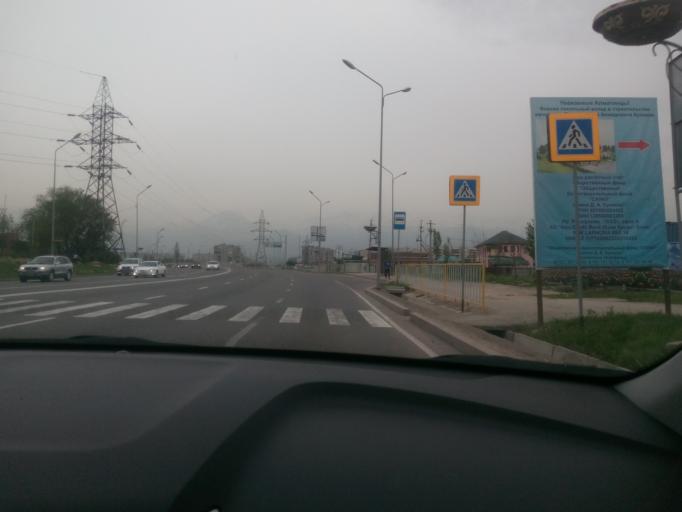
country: KZ
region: Almaty Qalasy
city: Almaty
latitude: 43.2488
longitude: 76.8252
